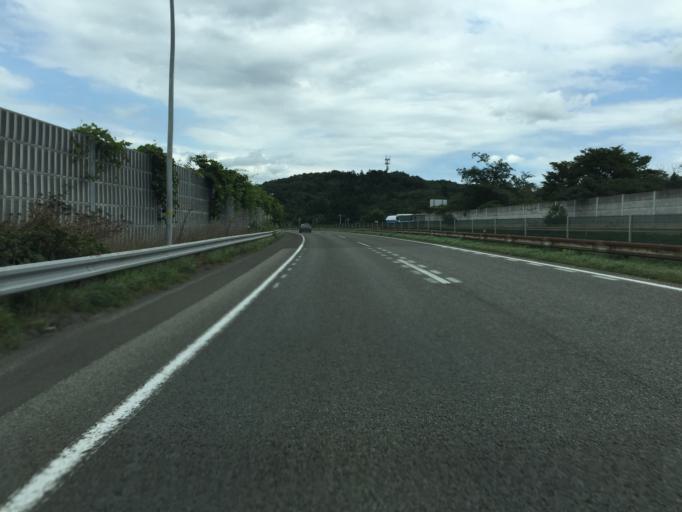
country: JP
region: Miyagi
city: Sendai
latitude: 38.1929
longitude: 140.7825
